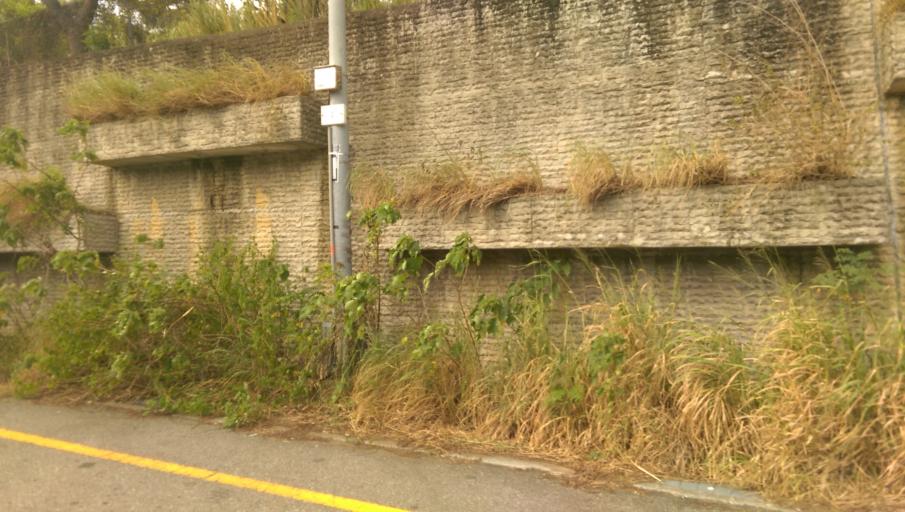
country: TW
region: Taiwan
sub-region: Hsinchu
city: Hsinchu
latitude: 24.7512
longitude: 120.9557
